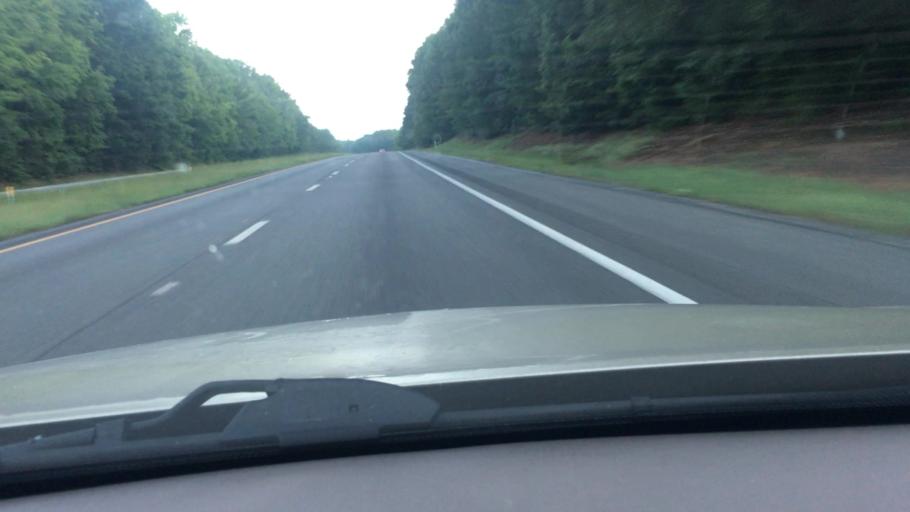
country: US
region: South Carolina
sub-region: Lexington County
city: Irmo
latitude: 34.1271
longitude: -81.2037
